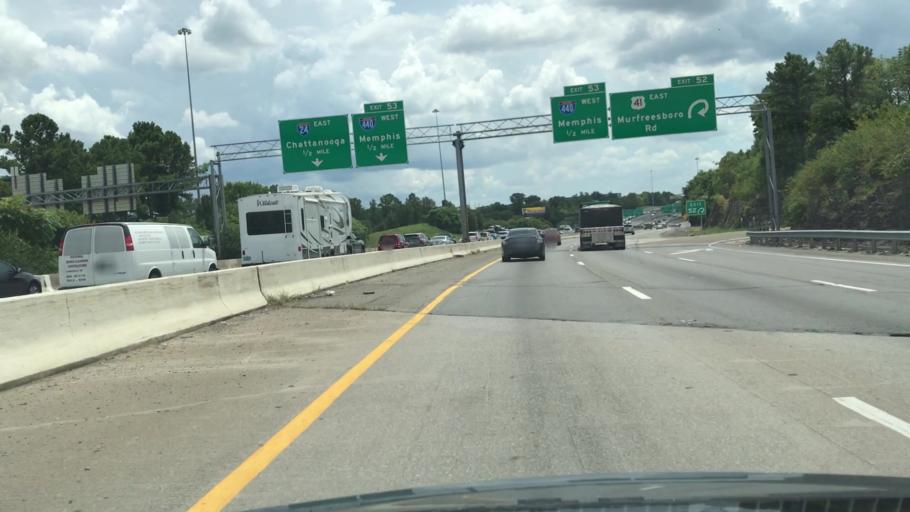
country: US
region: Tennessee
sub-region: Davidson County
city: Nashville
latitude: 36.1368
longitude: -86.7272
